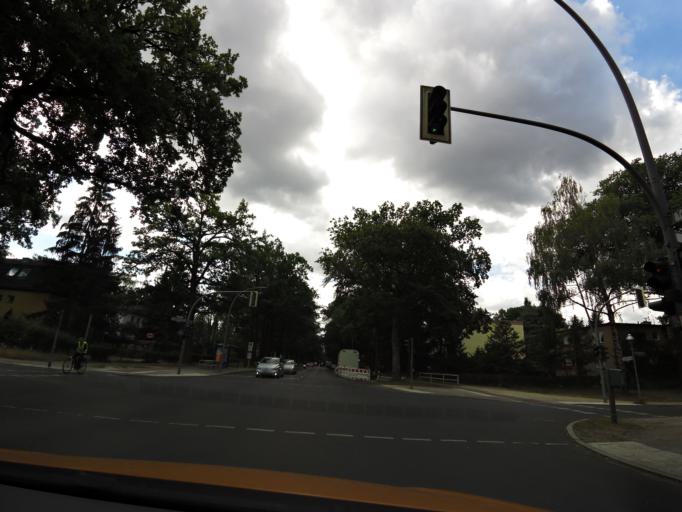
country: DE
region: Berlin
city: Zehlendorf Bezirk
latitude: 52.4222
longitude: 13.2637
